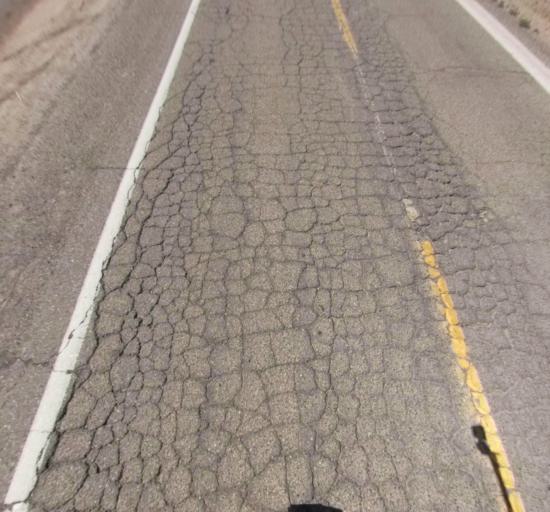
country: US
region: California
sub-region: Madera County
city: Fairmead
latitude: 36.9484
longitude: -120.2019
